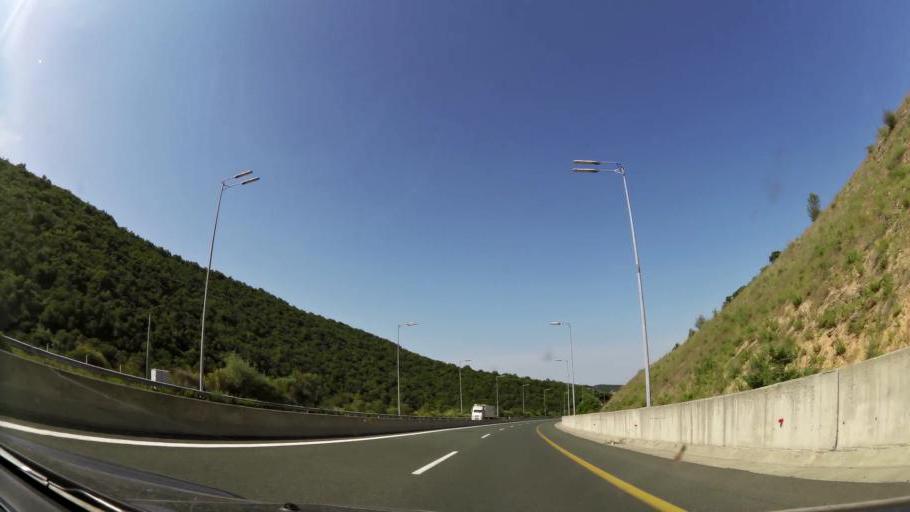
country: GR
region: Central Macedonia
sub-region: Nomos Imathias
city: Veroia
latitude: 40.4463
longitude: 22.2007
